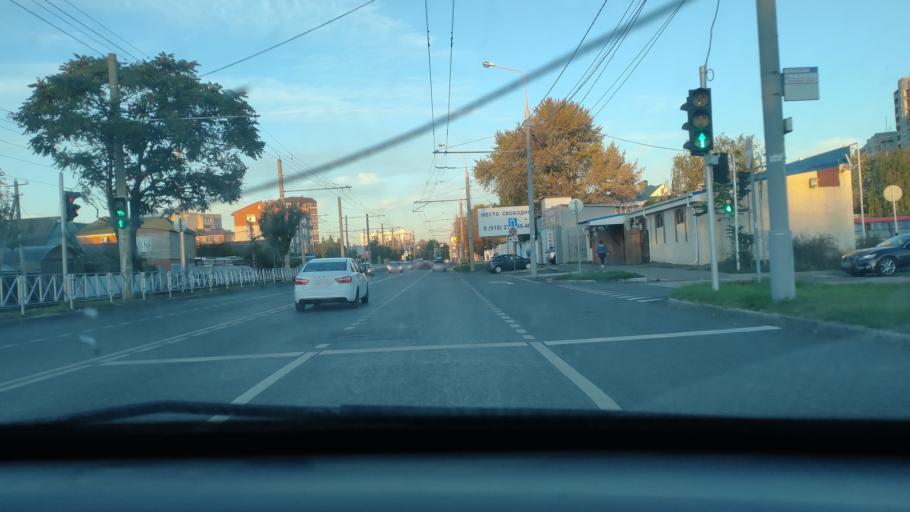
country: RU
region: Krasnodarskiy
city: Krasnodar
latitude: 45.0388
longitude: 38.9316
